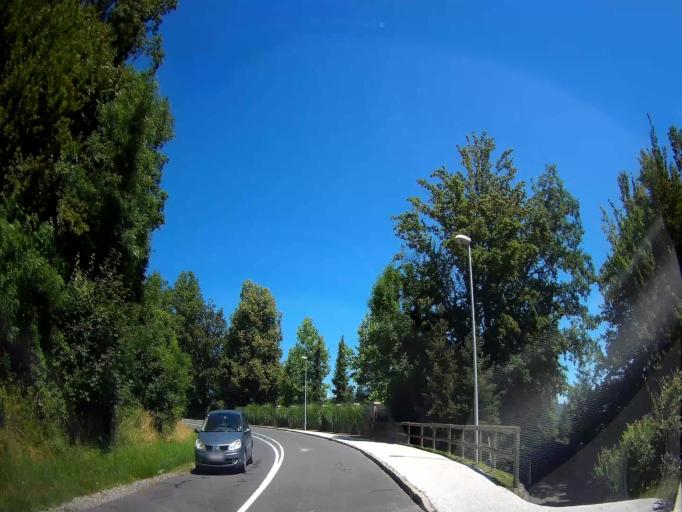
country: AT
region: Carinthia
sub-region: Politischer Bezirk Klagenfurt Land
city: Maria Worth
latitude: 46.6105
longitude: 14.1802
